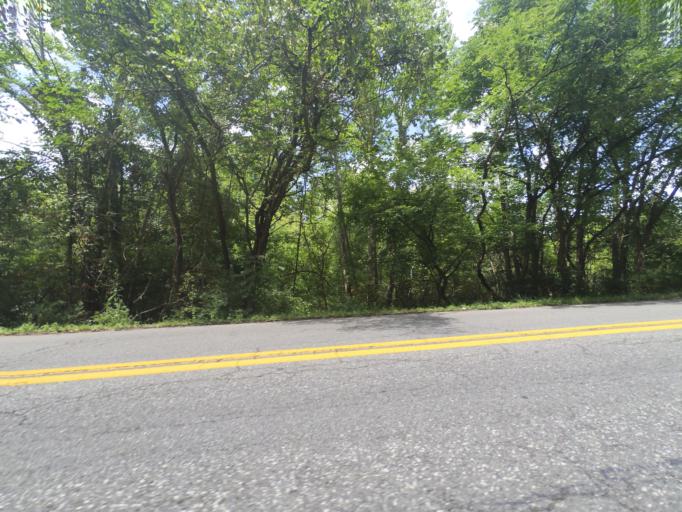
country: US
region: West Virginia
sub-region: Cabell County
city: Pea Ridge
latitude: 38.4085
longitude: -82.3717
